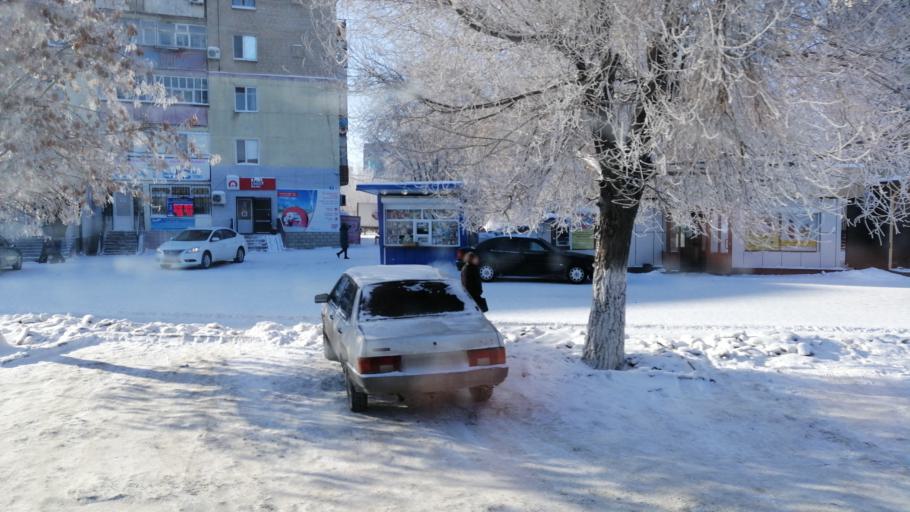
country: KZ
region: Aqtoebe
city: Aqtobe
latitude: 50.3024
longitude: 57.1531
